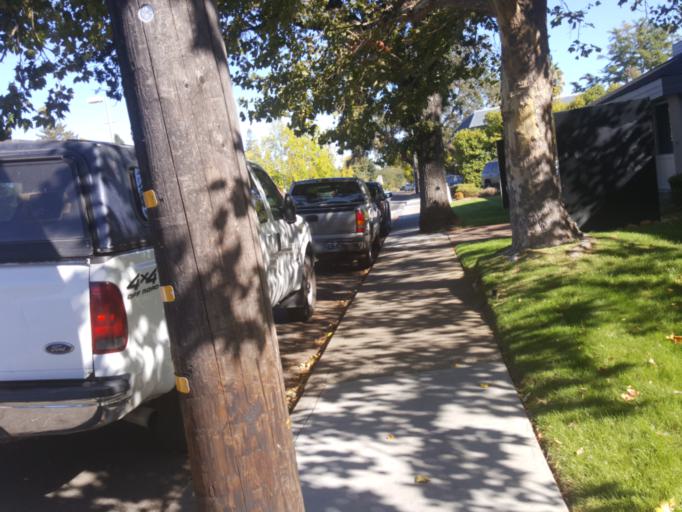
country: US
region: California
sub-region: Mendocino County
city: Ukiah
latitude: 39.1354
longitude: -123.2094
